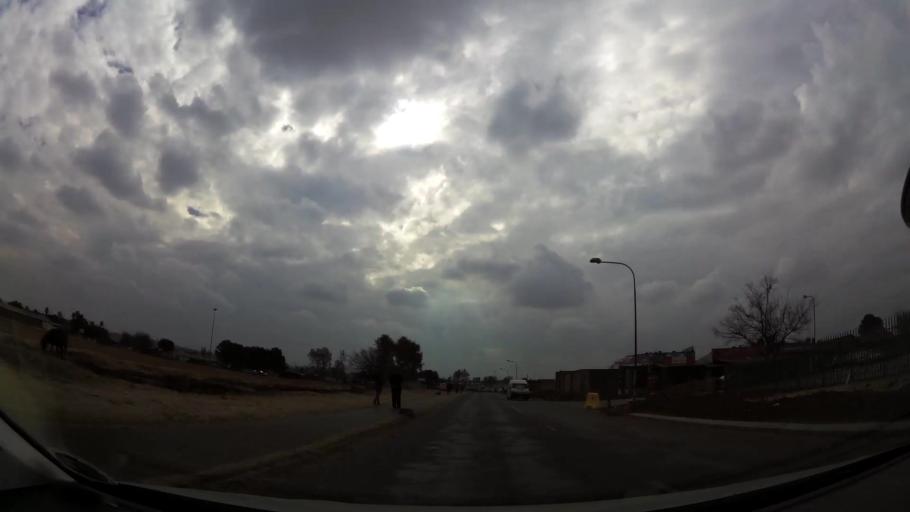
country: ZA
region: Gauteng
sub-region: City of Johannesburg Metropolitan Municipality
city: Soweto
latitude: -26.2650
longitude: 27.8487
